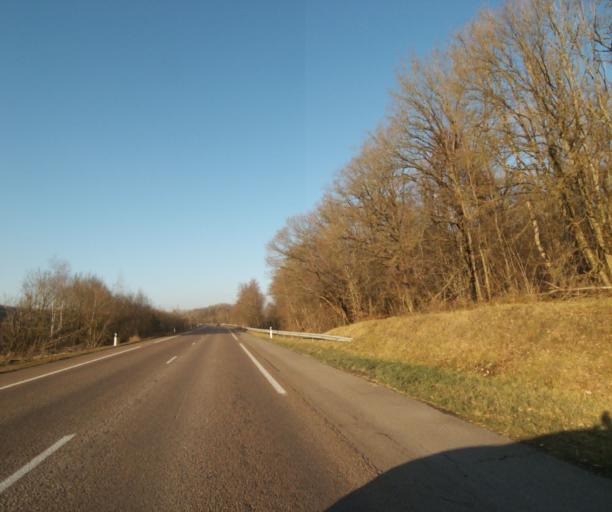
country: FR
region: Champagne-Ardenne
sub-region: Departement de la Haute-Marne
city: Chevillon
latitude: 48.4948
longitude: 5.1103
